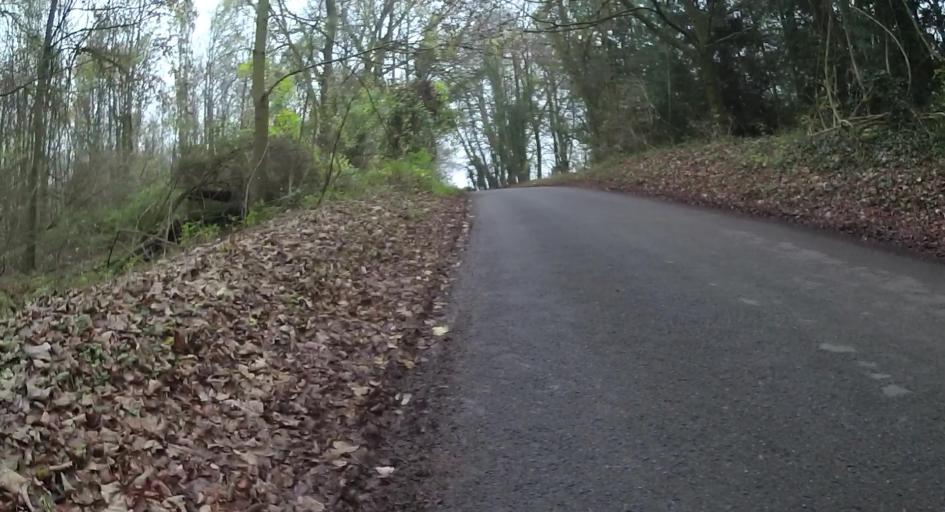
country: GB
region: England
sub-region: Hampshire
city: Kings Worthy
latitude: 51.1326
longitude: -1.2108
